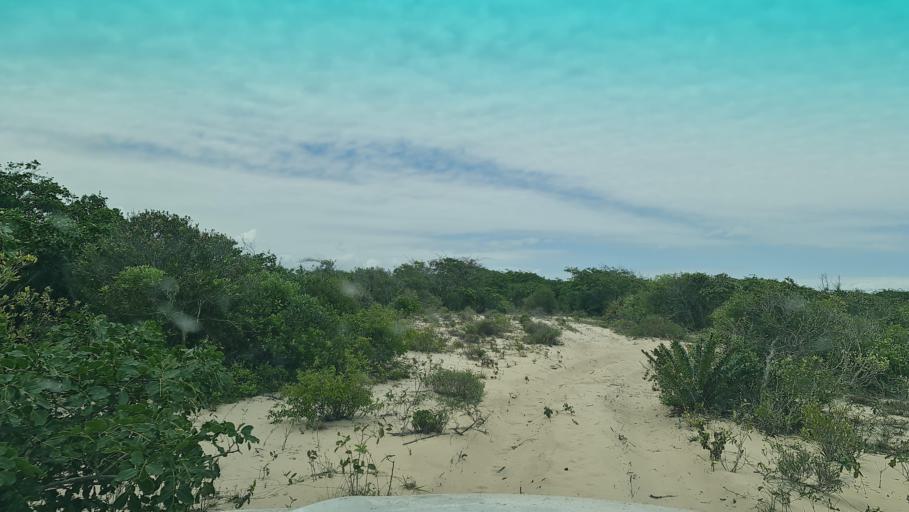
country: MZ
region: Maputo
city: Manhica
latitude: -25.6297
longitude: 32.7886
